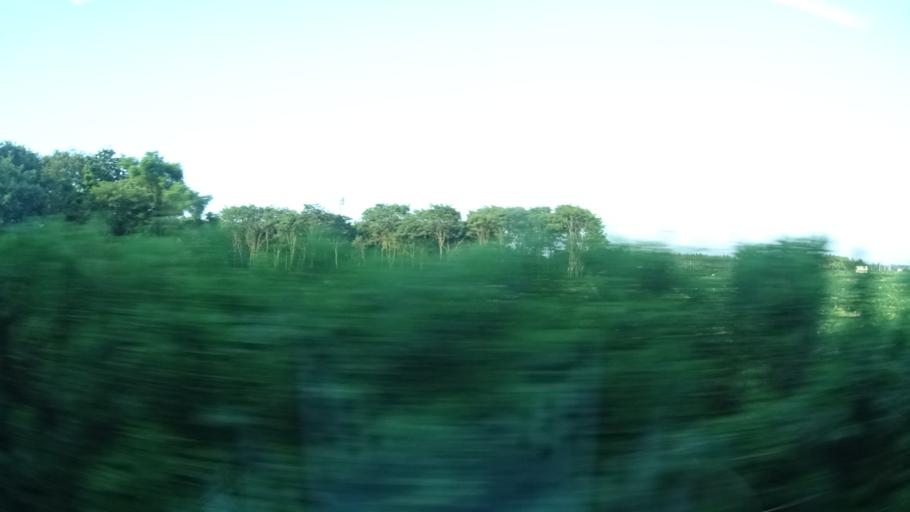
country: JP
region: Ibaraki
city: Tomobe
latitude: 36.2765
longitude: 140.2796
